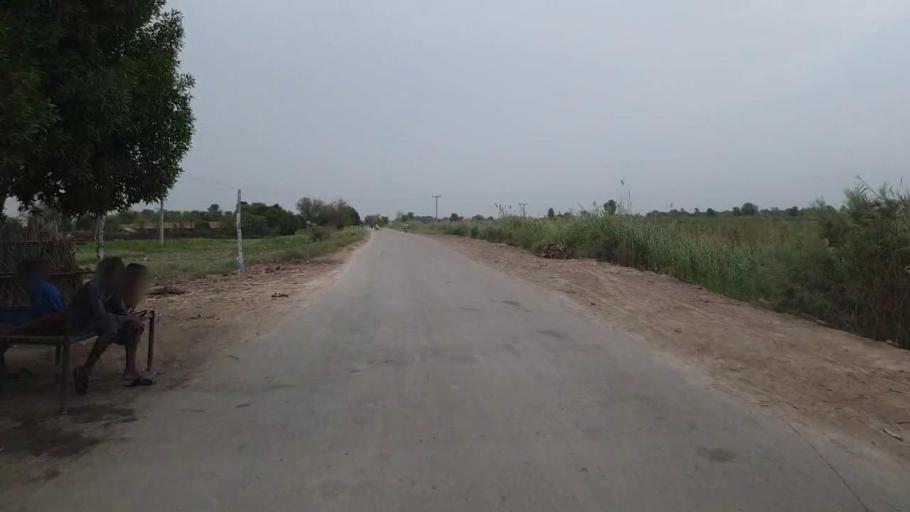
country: PK
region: Sindh
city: Bandhi
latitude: 26.5378
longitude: 68.2195
